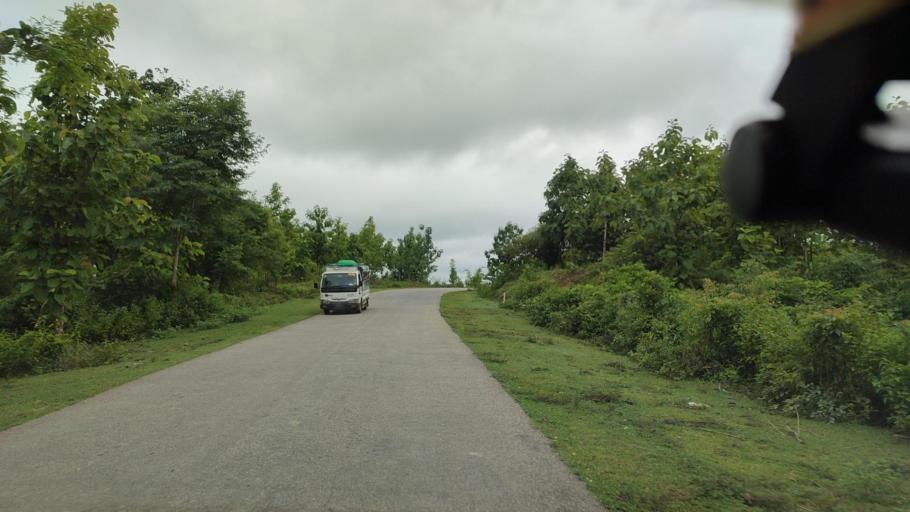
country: MM
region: Mandalay
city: Nay Pyi Taw
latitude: 19.9905
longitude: 95.9008
